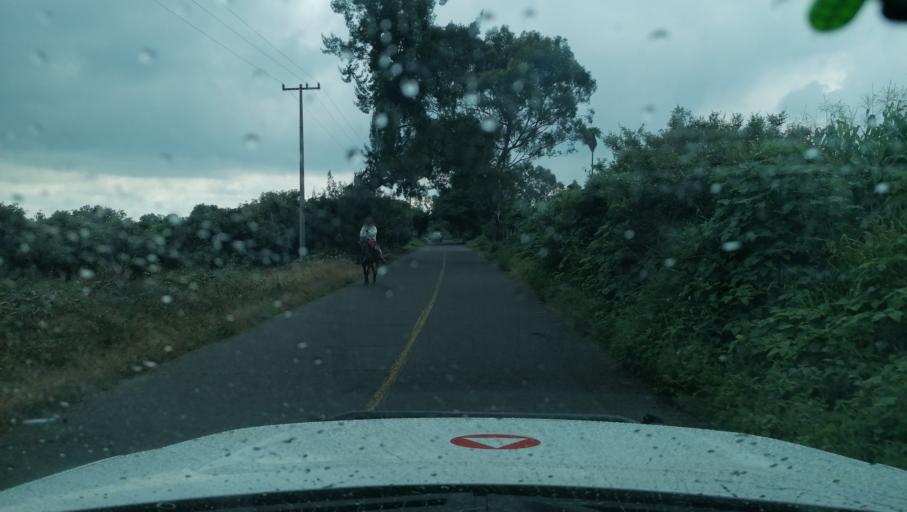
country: MX
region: Morelos
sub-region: Yecapixtla
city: Texcala
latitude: 18.9317
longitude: -98.8058
